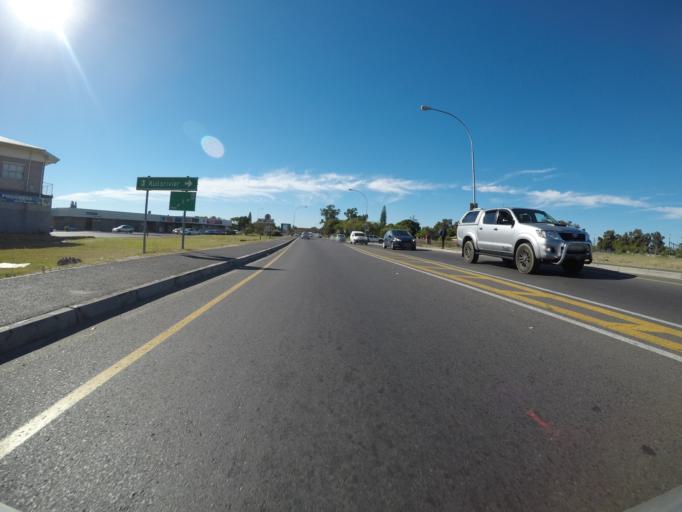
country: ZA
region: Western Cape
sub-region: City of Cape Town
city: Kraaifontein
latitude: -33.9356
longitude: 18.6767
